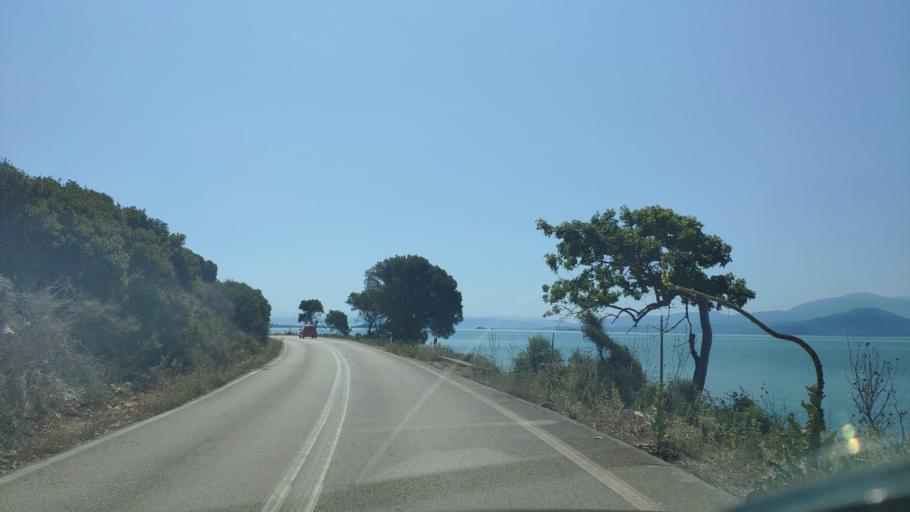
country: GR
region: Epirus
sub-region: Nomos Artas
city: Aneza
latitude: 39.0319
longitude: 20.8623
